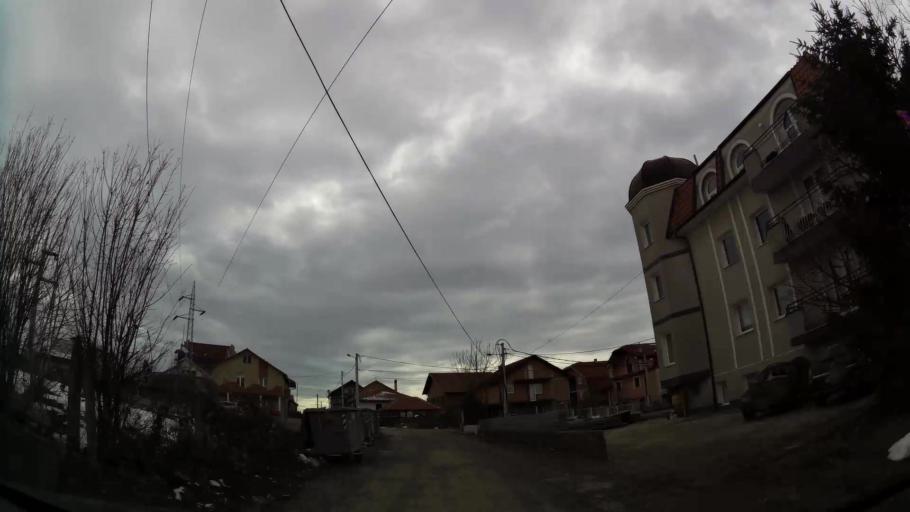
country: RS
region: Central Serbia
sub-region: Belgrade
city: Rakovica
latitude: 44.7426
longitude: 20.3994
